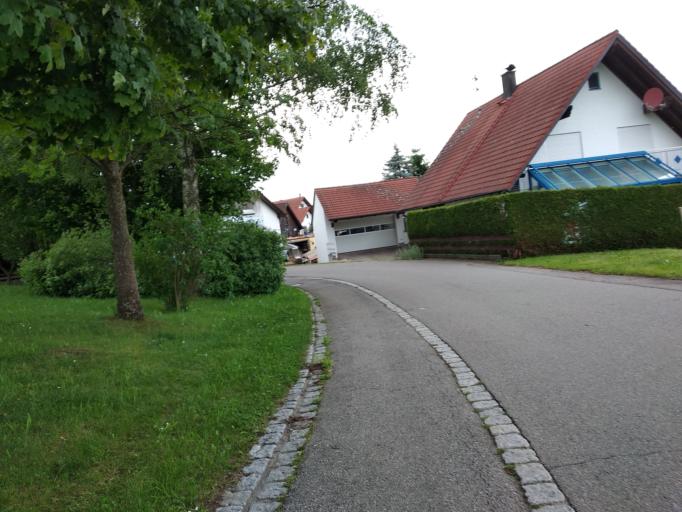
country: DE
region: Bavaria
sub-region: Swabia
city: Lachen
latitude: 47.9454
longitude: 10.2237
